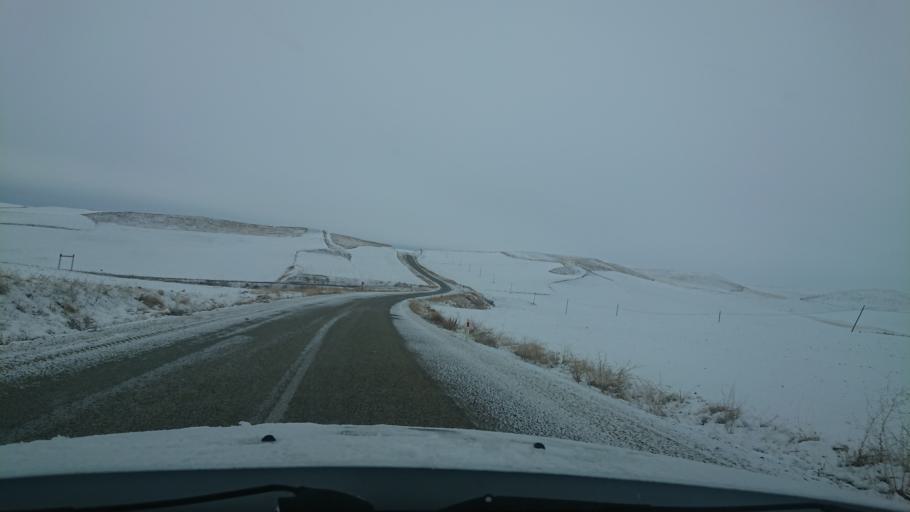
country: TR
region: Aksaray
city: Agacoren
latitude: 38.7856
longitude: 33.8711
